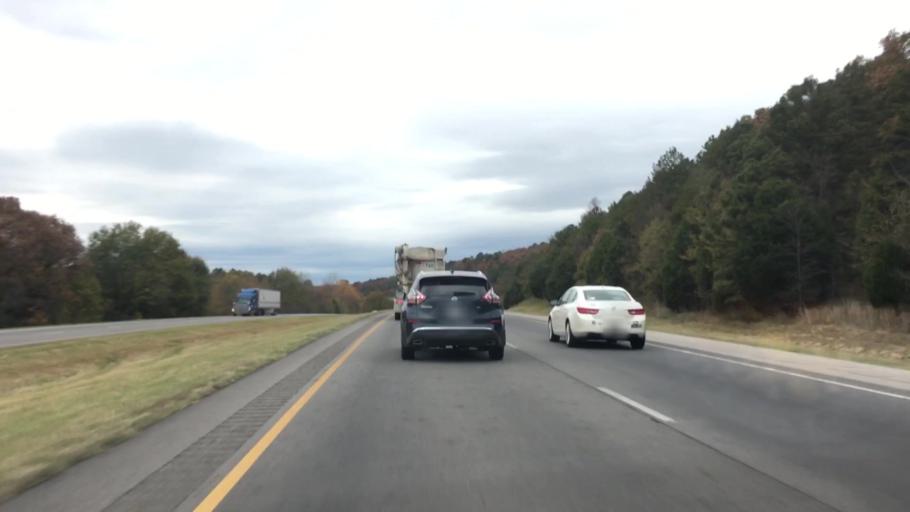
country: US
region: Arkansas
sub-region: Johnson County
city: Coal Hill
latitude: 35.5009
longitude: -93.7233
